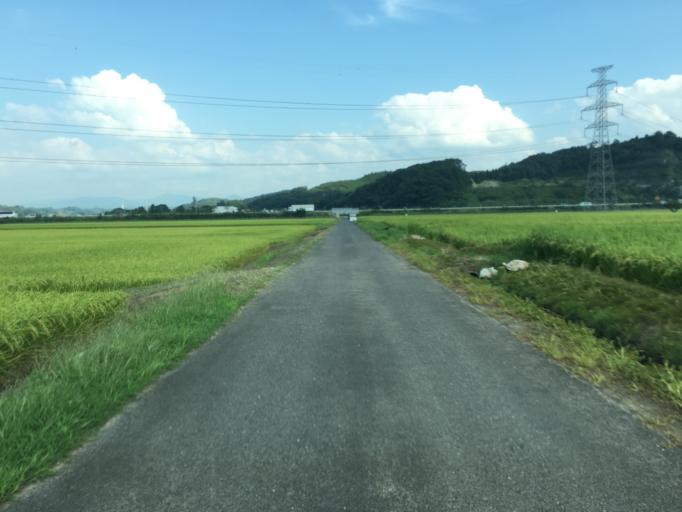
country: JP
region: Fukushima
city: Motomiya
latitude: 37.5541
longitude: 140.3894
